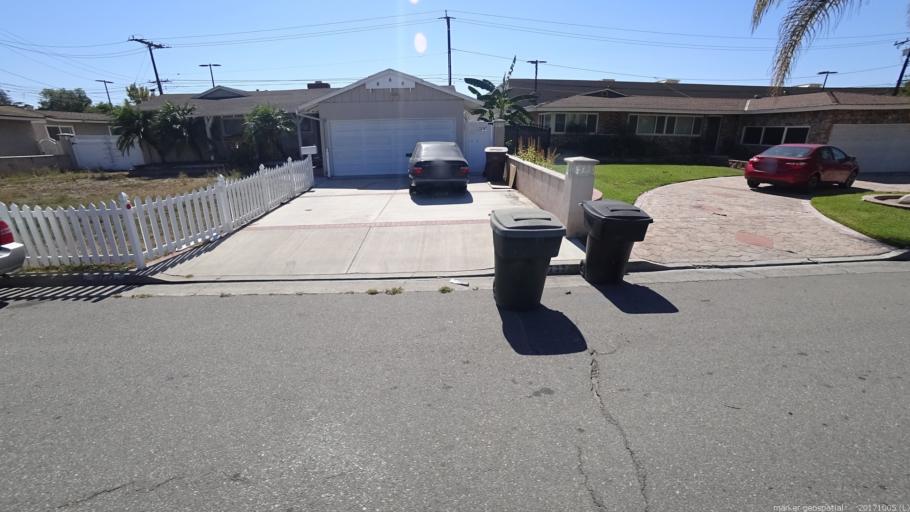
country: US
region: California
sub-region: Orange County
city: Garden Grove
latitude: 33.7916
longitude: -117.9635
